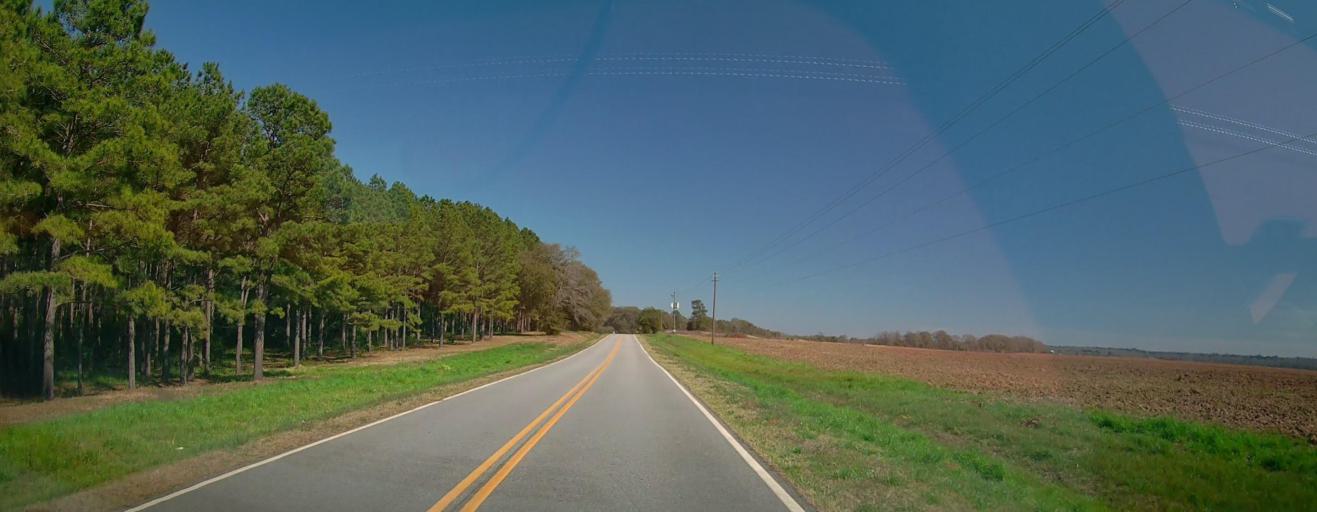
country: US
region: Georgia
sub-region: Houston County
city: Perry
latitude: 32.4385
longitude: -83.7327
